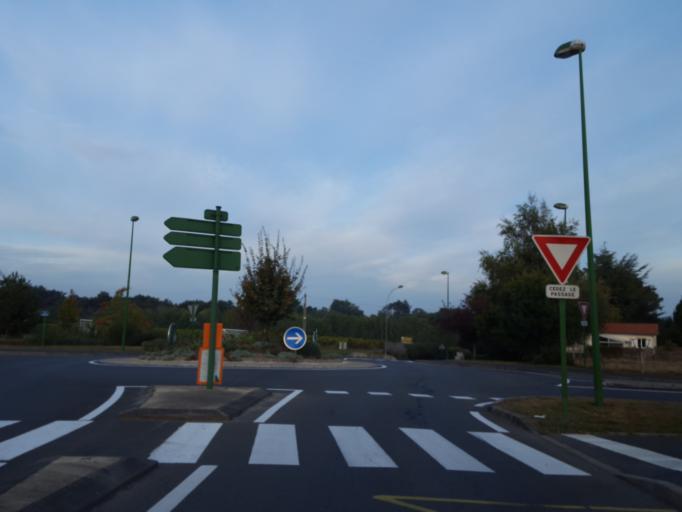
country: FR
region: Pays de la Loire
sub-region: Departement de la Loire-Atlantique
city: Haute-Goulaine
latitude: 47.2005
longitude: -1.4438
